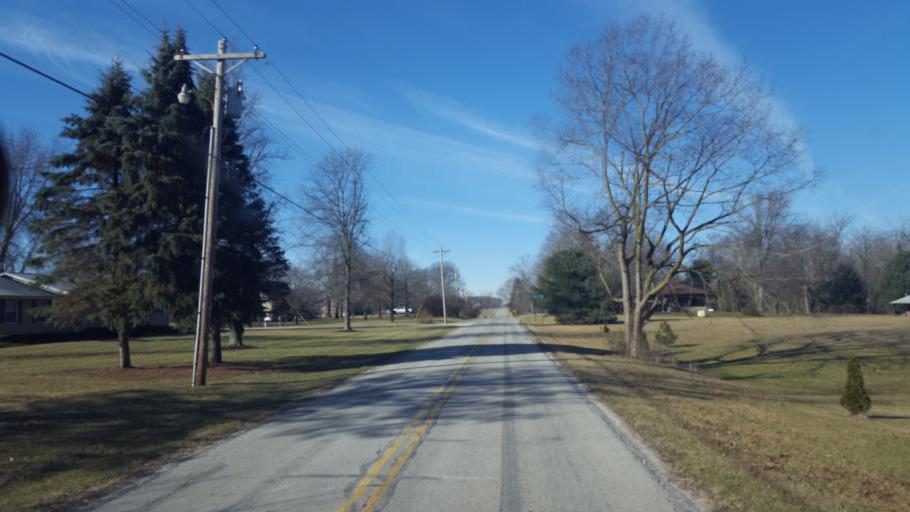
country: US
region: Ohio
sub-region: Morrow County
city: Cardington
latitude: 40.5280
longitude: -83.0103
